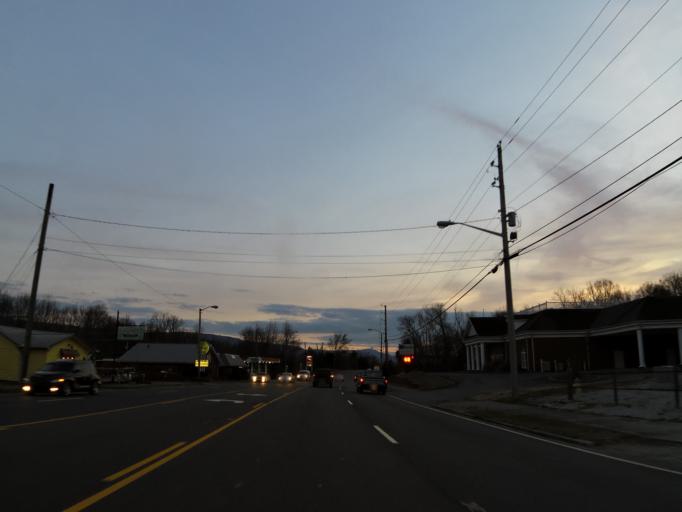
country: US
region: Tennessee
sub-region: McMinn County
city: Etowah
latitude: 35.3338
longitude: -84.5203
